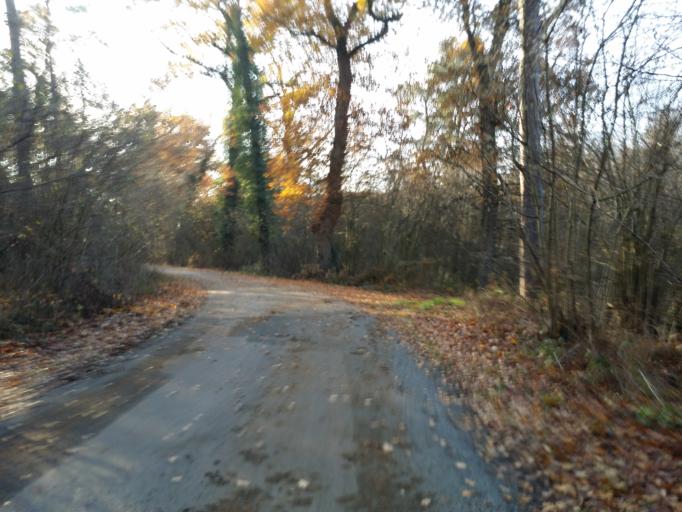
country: DE
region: Lower Saxony
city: Ahausen
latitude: 53.0986
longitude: 9.3484
